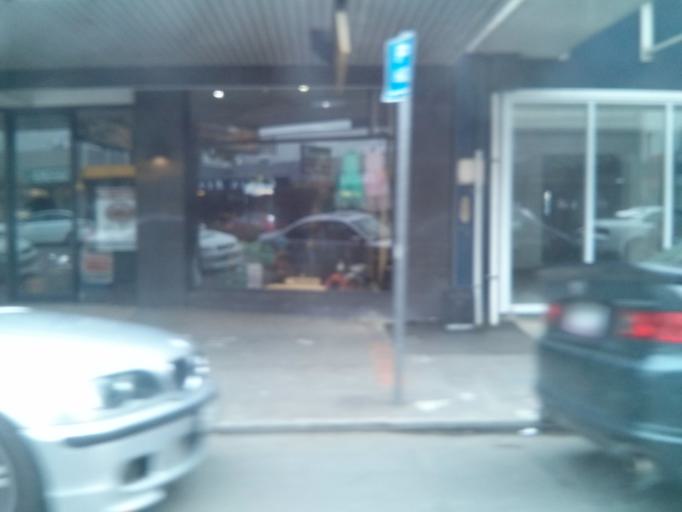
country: NZ
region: Canterbury
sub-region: Christchurch City
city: Christchurch
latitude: -43.5298
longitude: 172.5993
